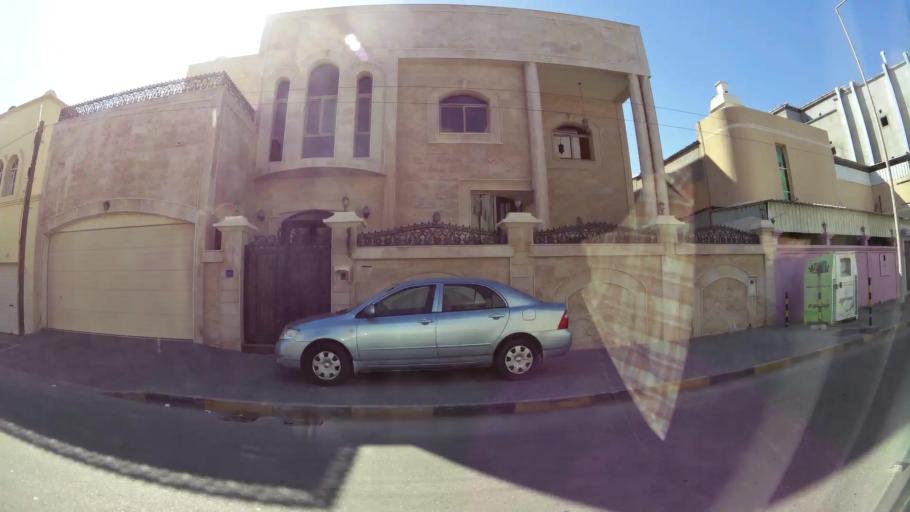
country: BH
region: Muharraq
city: Al Hadd
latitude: 26.2350
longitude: 50.6554
